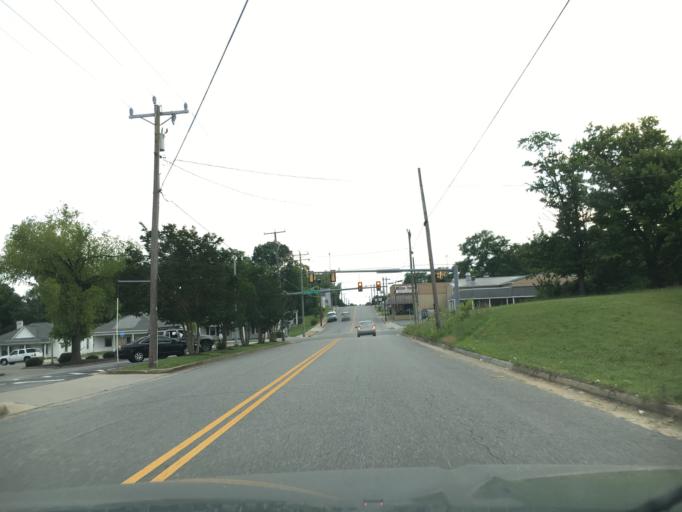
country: US
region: Virginia
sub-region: Halifax County
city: South Boston
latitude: 36.7036
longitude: -78.9063
